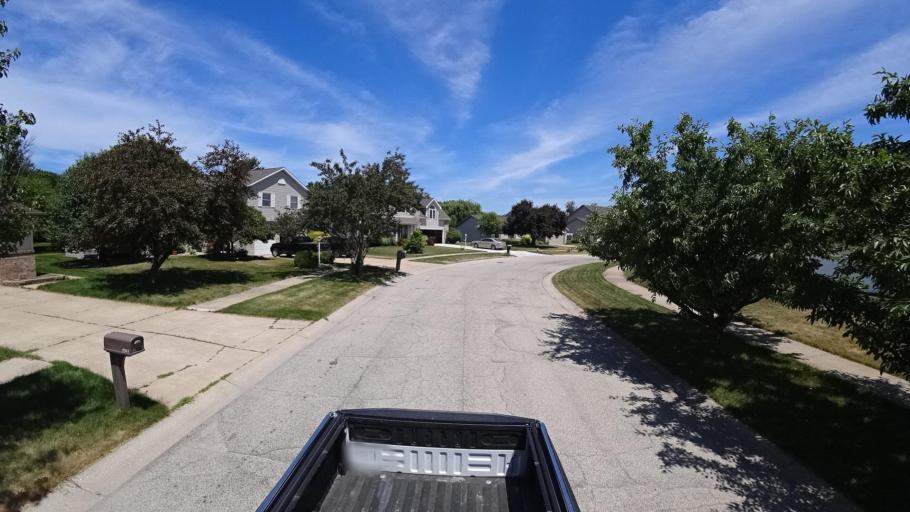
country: US
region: Indiana
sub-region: Porter County
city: Porter
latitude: 41.6053
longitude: -87.0947
